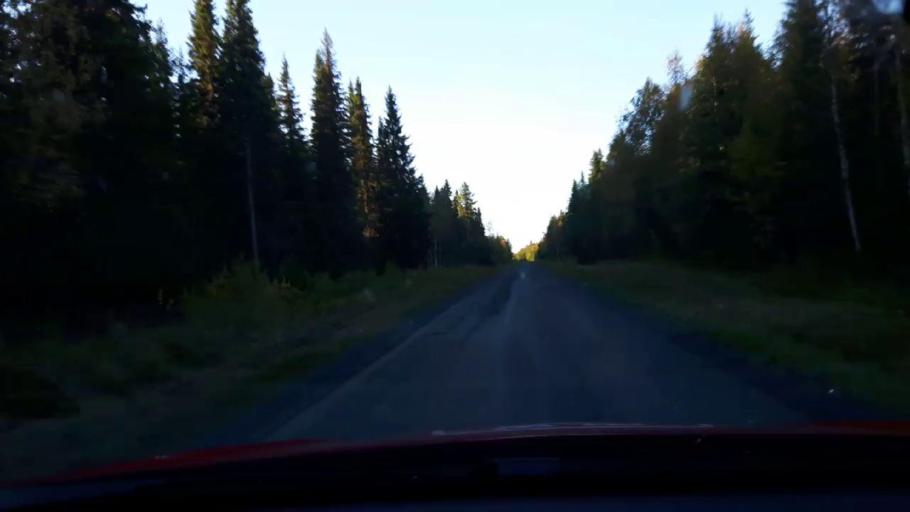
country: SE
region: Jaemtland
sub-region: Krokoms Kommun
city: Krokom
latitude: 63.4322
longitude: 14.6094
